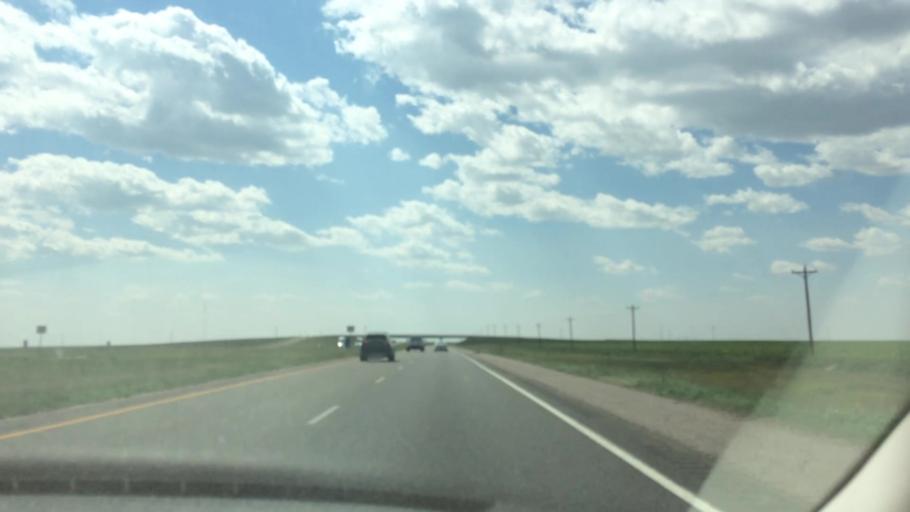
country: US
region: Colorado
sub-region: Lincoln County
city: Hugo
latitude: 39.2877
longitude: -103.0919
